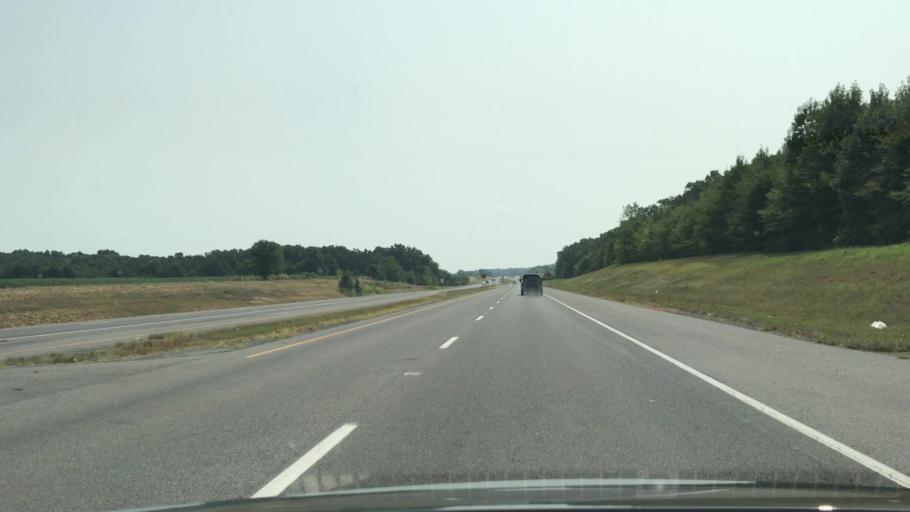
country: US
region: Kentucky
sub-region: Calloway County
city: Murray
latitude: 36.6506
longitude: -88.2675
